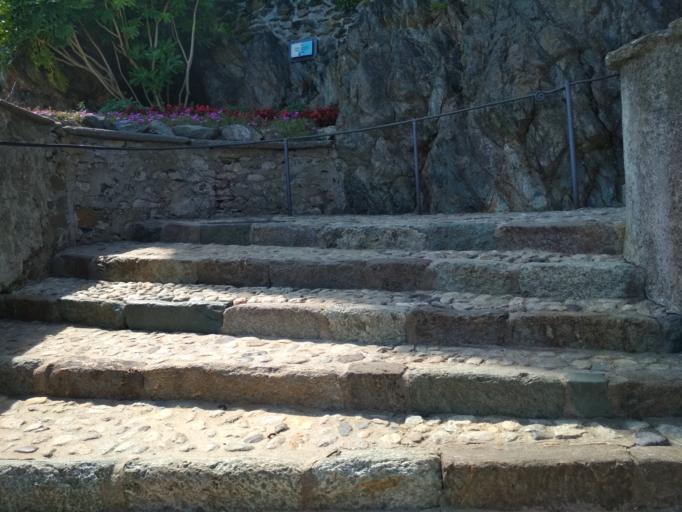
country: IT
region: Piedmont
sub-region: Provincia di Torino
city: Chiusa di San Michele
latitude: 45.0977
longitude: 7.3432
